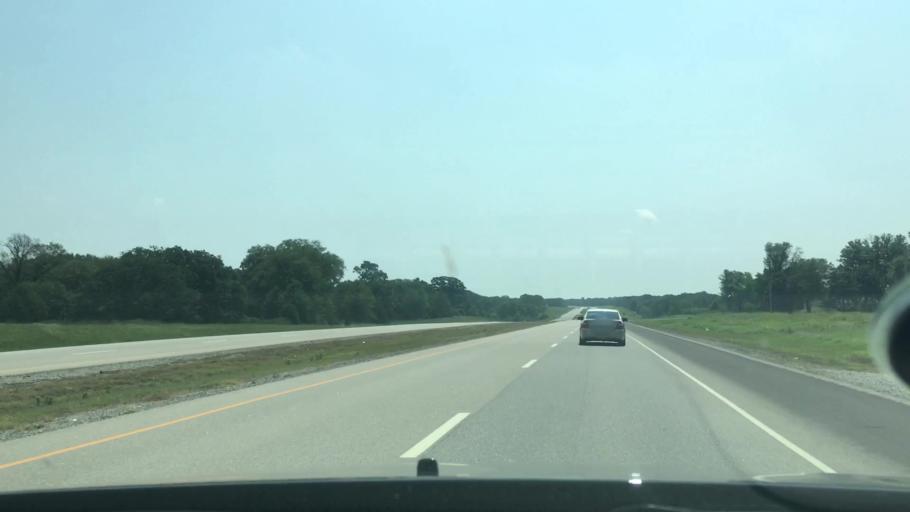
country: US
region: Oklahoma
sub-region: Atoka County
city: Atoka
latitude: 34.3285
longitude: -96.0474
